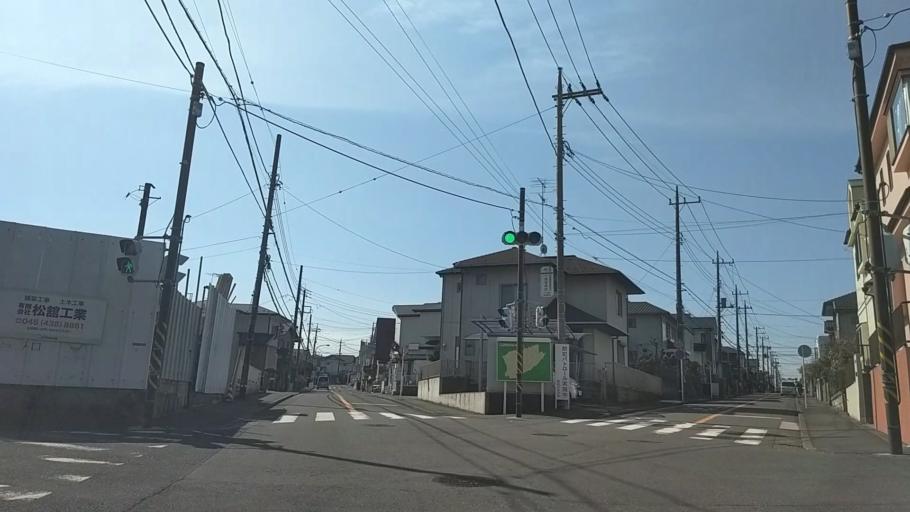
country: JP
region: Kanagawa
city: Kamakura
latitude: 35.3958
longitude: 139.5565
